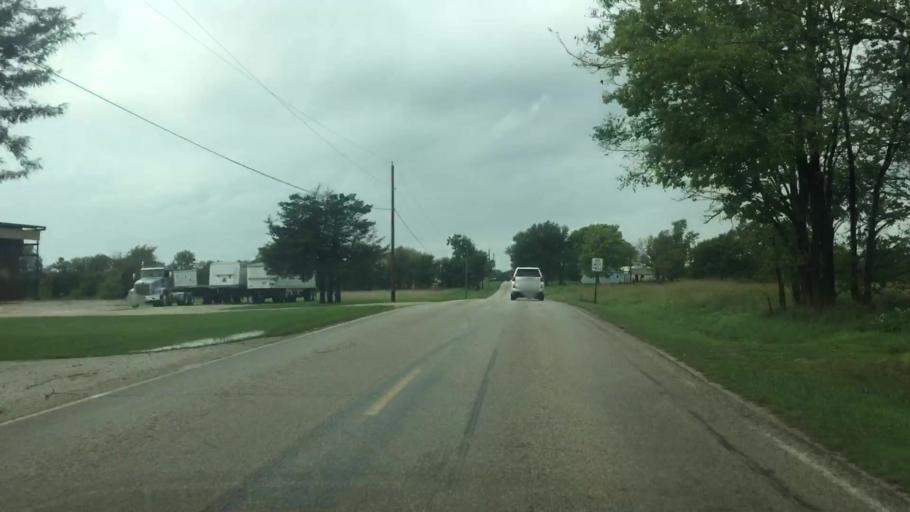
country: US
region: Kansas
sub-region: Allen County
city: Iola
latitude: 37.8857
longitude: -95.4207
